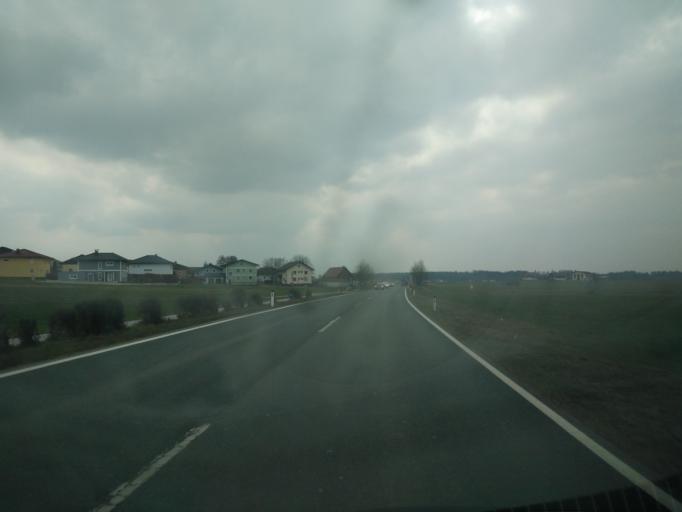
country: AT
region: Salzburg
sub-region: Politischer Bezirk Salzburg-Umgebung
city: Lamprechtshausen
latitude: 47.9788
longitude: 12.9525
